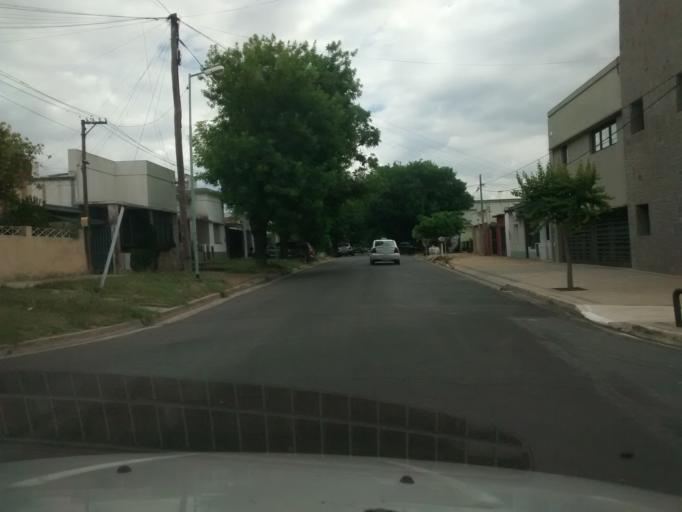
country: AR
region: Buenos Aires
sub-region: Partido de La Plata
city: La Plata
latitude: -34.9299
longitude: -57.9225
